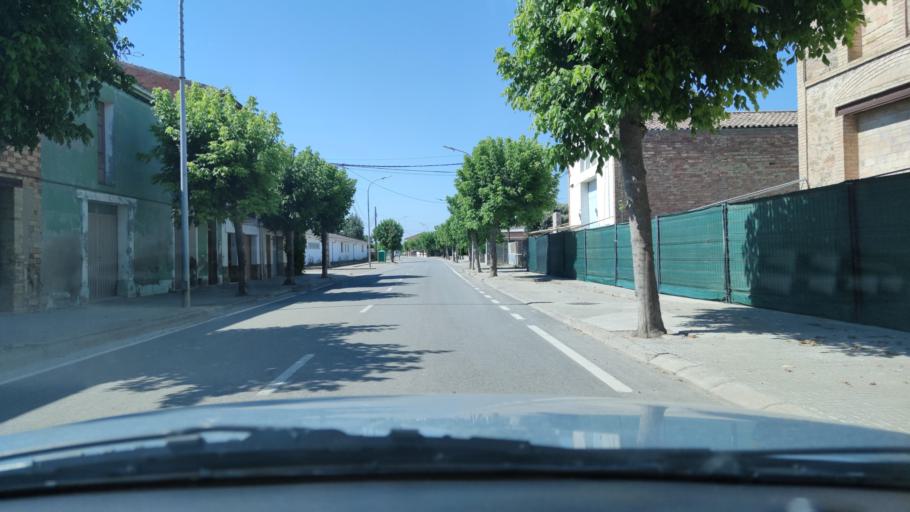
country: ES
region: Catalonia
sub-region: Provincia de Lleida
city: Castellsera
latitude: 41.7440
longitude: 0.9870
